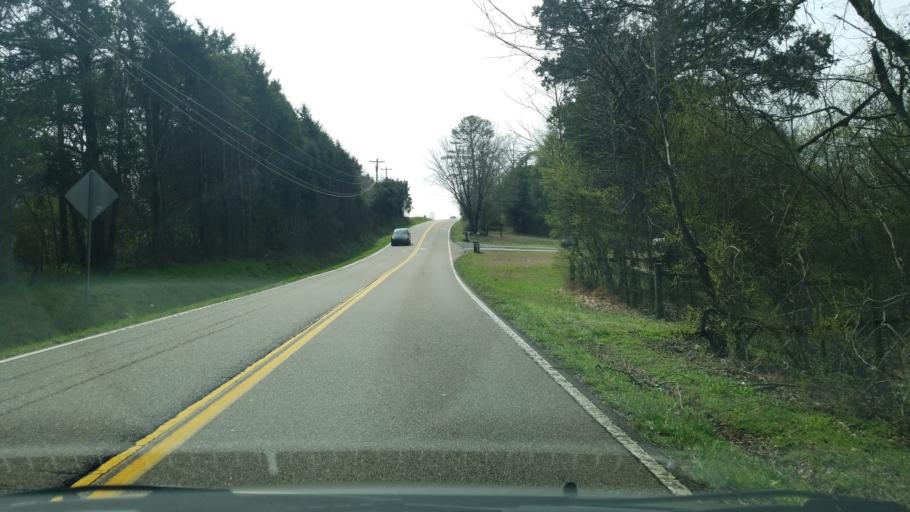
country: US
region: Tennessee
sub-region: Hamilton County
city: Collegedale
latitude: 35.1098
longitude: -85.0663
